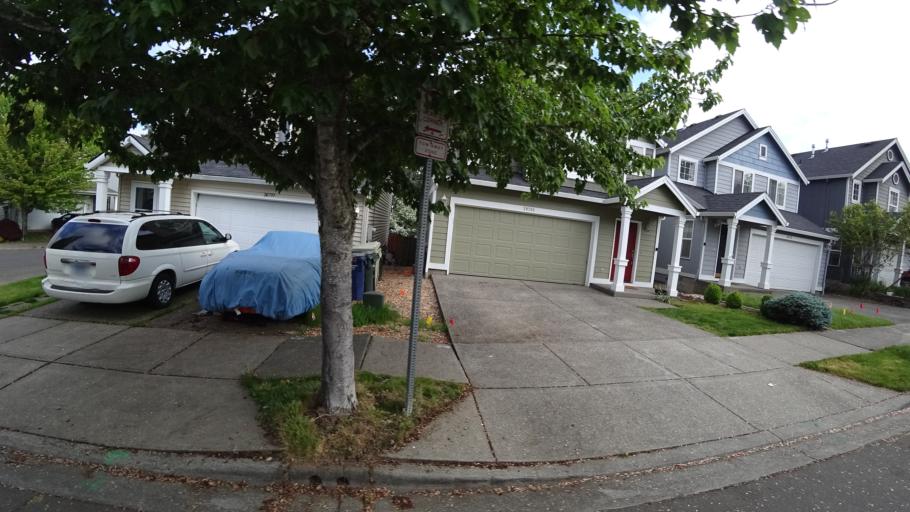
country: US
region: Oregon
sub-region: Washington County
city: Aloha
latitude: 45.5186
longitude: -122.8909
